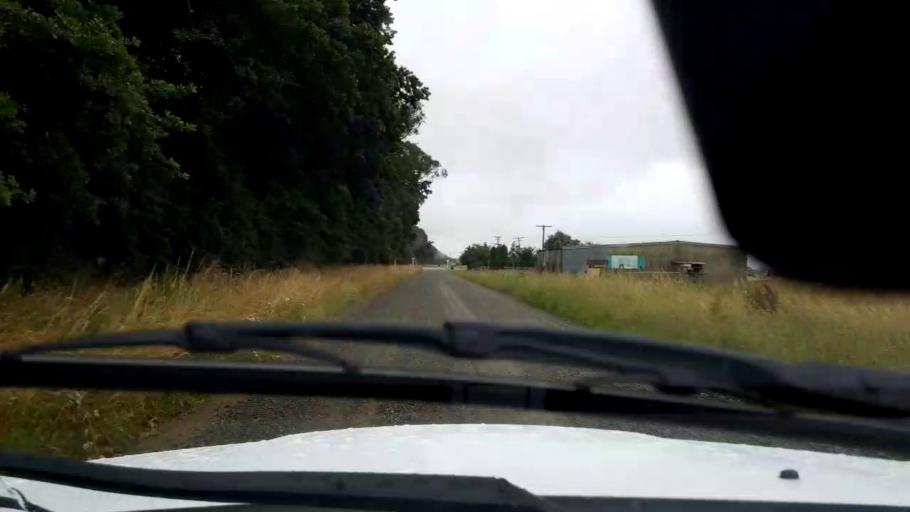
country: NZ
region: Canterbury
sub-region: Timaru District
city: Pleasant Point
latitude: -44.1939
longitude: 171.2816
